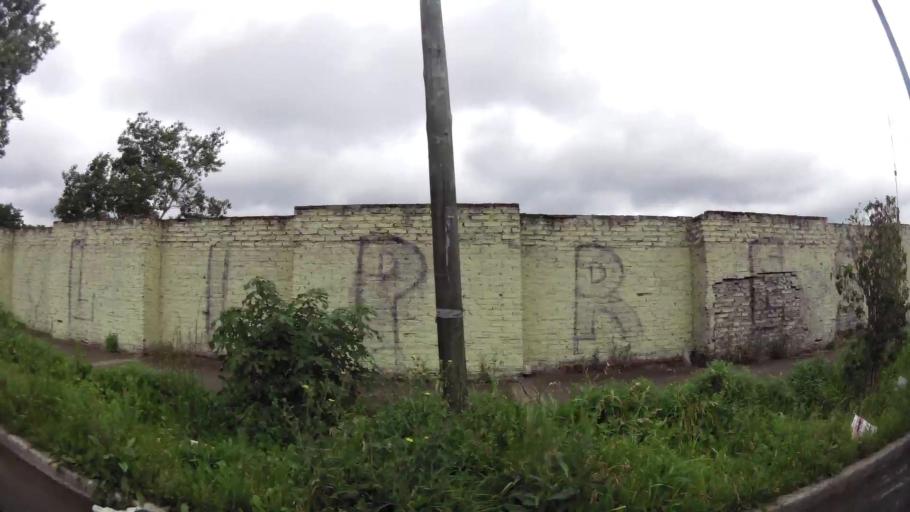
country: AR
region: Buenos Aires
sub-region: Partido de Lanus
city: Lanus
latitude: -34.7291
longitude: -58.3778
